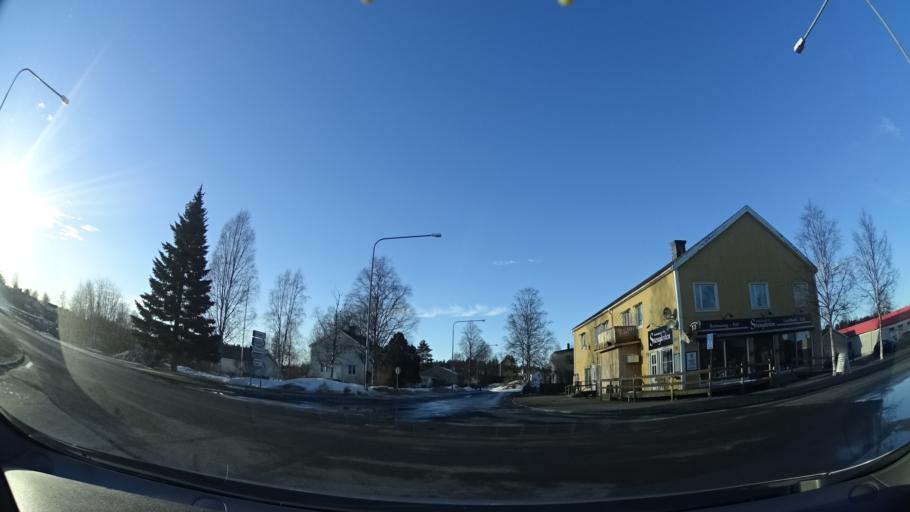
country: SE
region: Vaesterbotten
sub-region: Skelleftea Kommun
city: Byske
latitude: 64.9519
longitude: 21.2023
